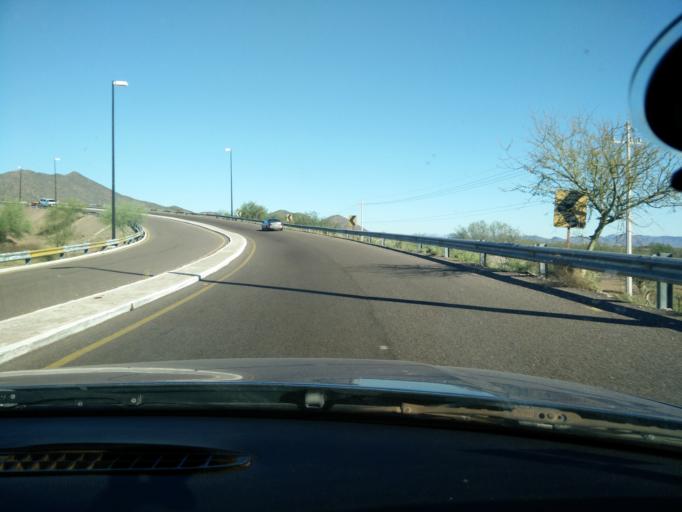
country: MX
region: Sonora
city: Heroica Guaymas
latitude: 27.9860
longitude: -110.9392
